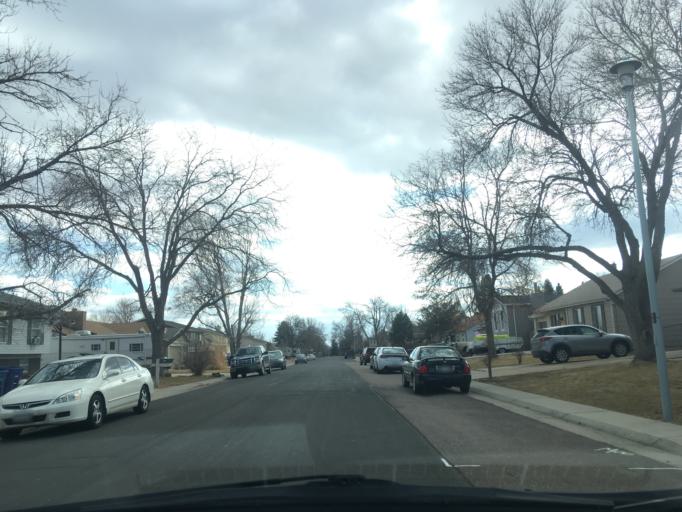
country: US
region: Colorado
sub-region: Broomfield County
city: Broomfield
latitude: 39.9404
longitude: -105.0550
